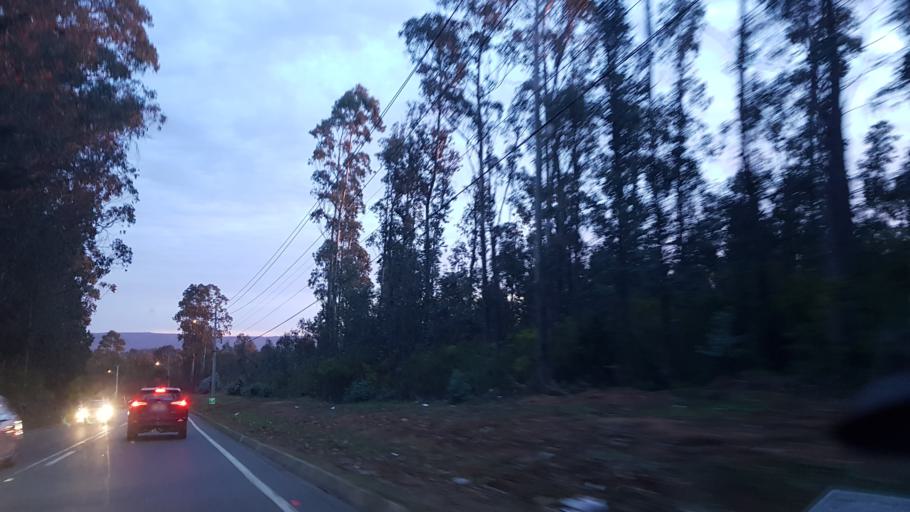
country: CL
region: Valparaiso
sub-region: Provincia de Valparaiso
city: Valparaiso
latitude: -33.0730
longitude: -71.6406
